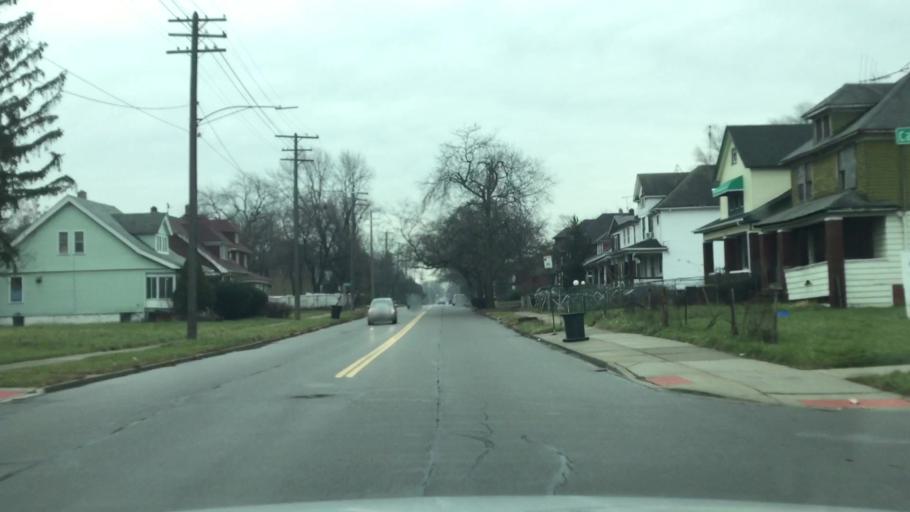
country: US
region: Michigan
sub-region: Wayne County
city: Hamtramck
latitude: 42.3719
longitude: -83.0096
